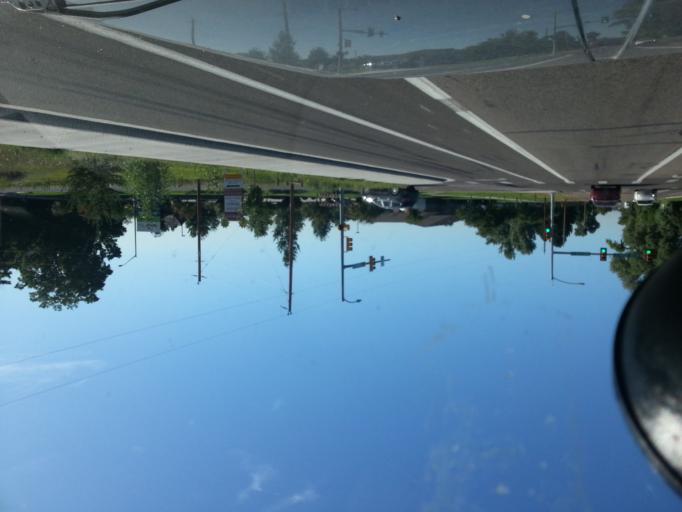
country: US
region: Colorado
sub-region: Larimer County
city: Fort Collins
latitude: 40.5087
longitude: -105.0392
